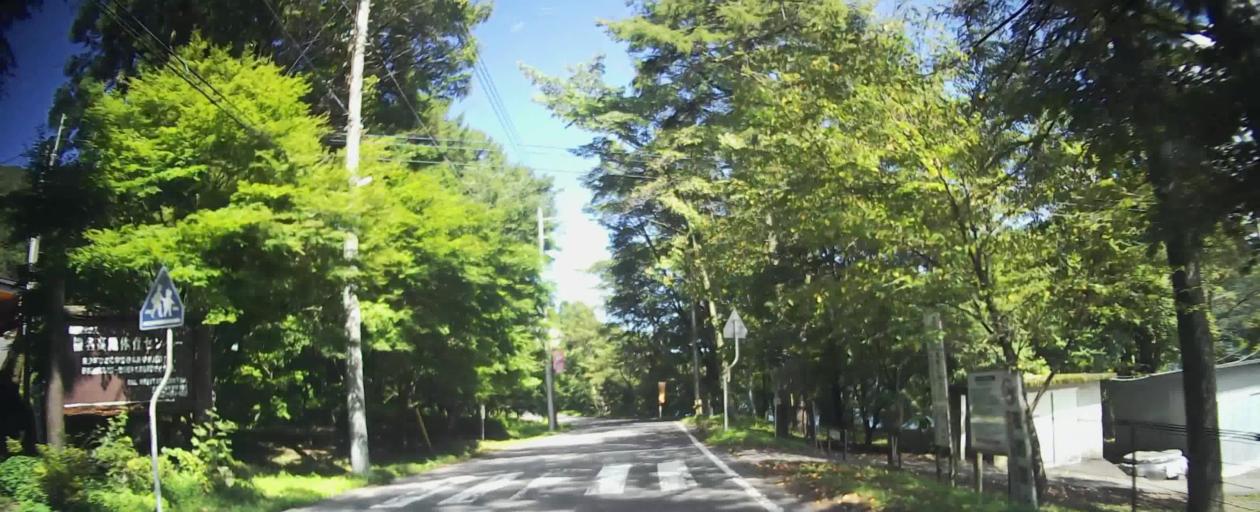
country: JP
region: Gunma
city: Nakanojomachi
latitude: 36.4789
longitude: 138.8619
